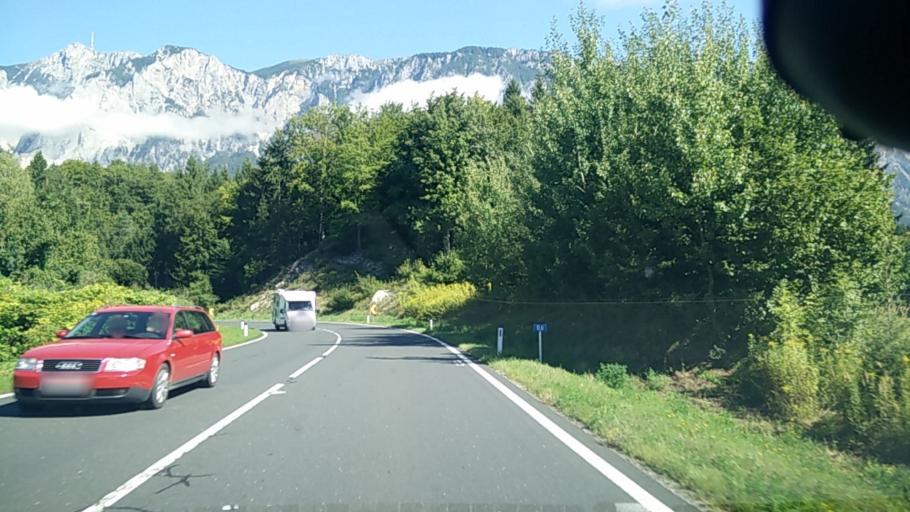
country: AT
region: Carinthia
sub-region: Politischer Bezirk Villach Land
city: Arnoldstein
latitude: 46.5598
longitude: 13.6977
